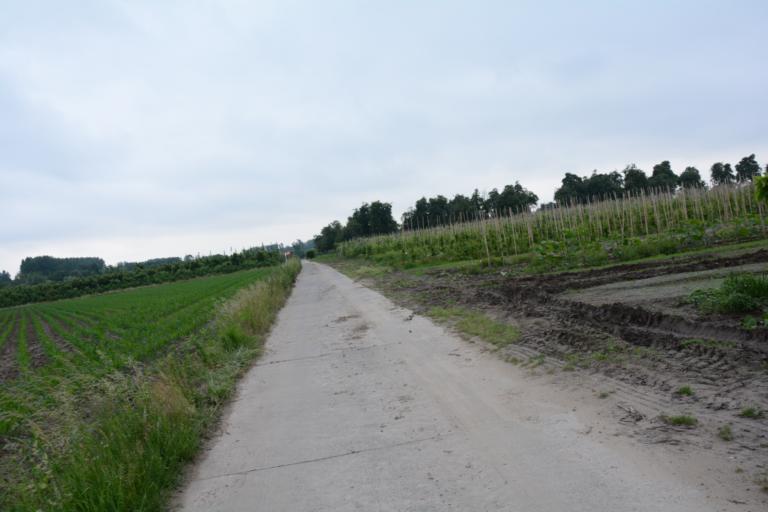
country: BE
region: Flanders
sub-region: Provincie Oost-Vlaanderen
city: Melle
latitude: 50.9885
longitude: 3.8024
